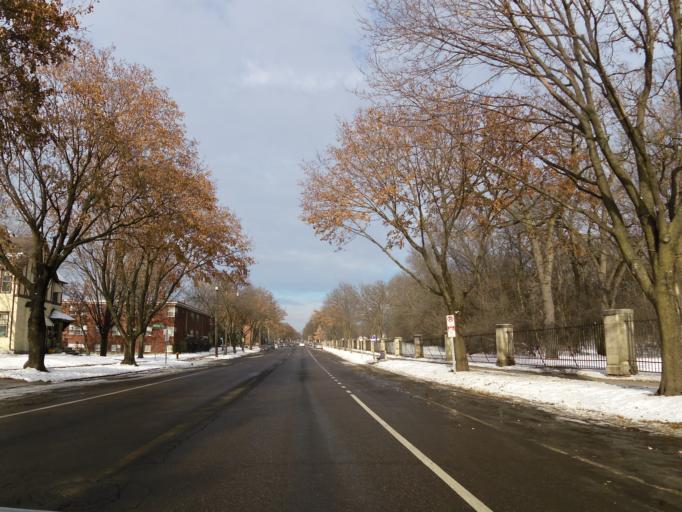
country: US
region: Minnesota
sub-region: Dakota County
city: Mendota Heights
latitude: 44.9228
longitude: -93.1874
